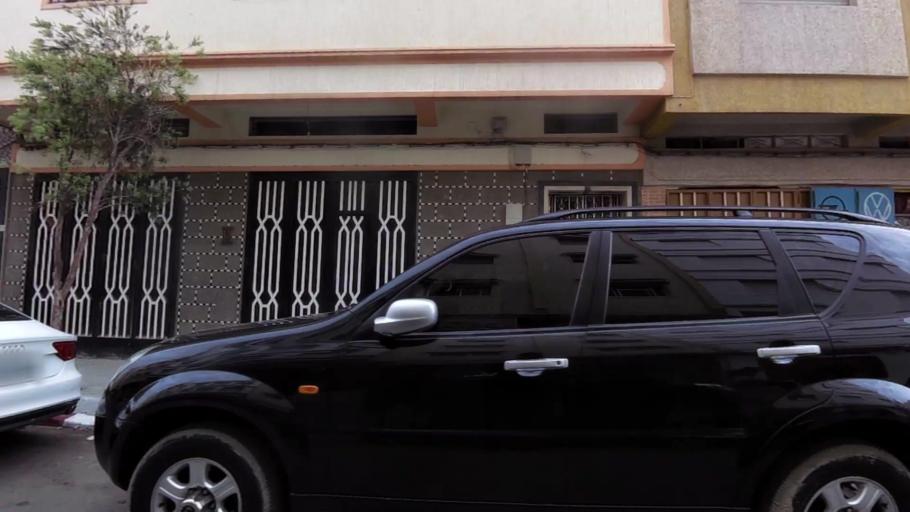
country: MA
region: Tanger-Tetouan
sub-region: Tanger-Assilah
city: Tangier
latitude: 35.7568
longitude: -5.7940
